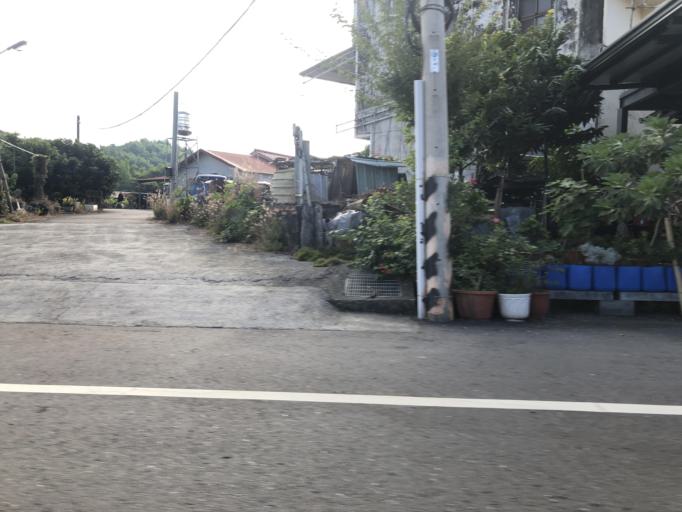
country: TW
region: Taiwan
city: Yujing
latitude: 23.0509
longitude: 120.4200
